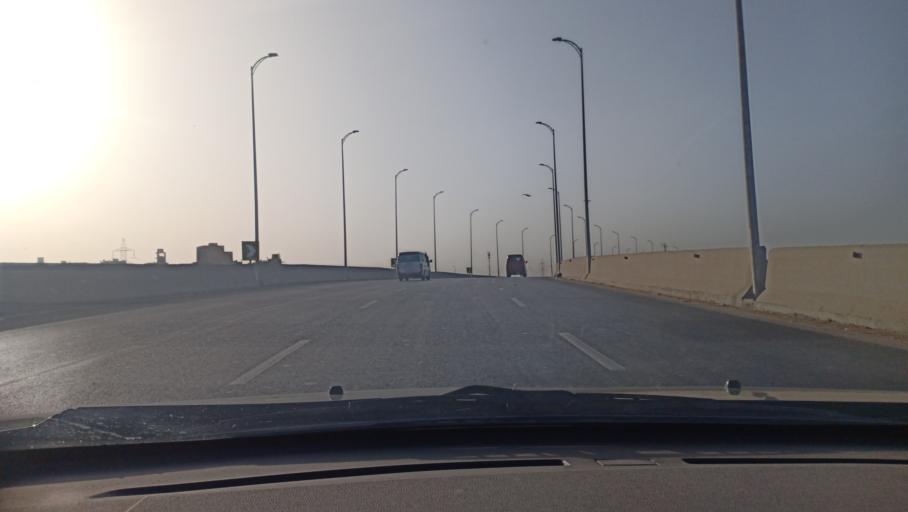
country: EG
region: Muhafazat al Qalyubiyah
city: Qalyub
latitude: 30.1474
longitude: 31.2566
